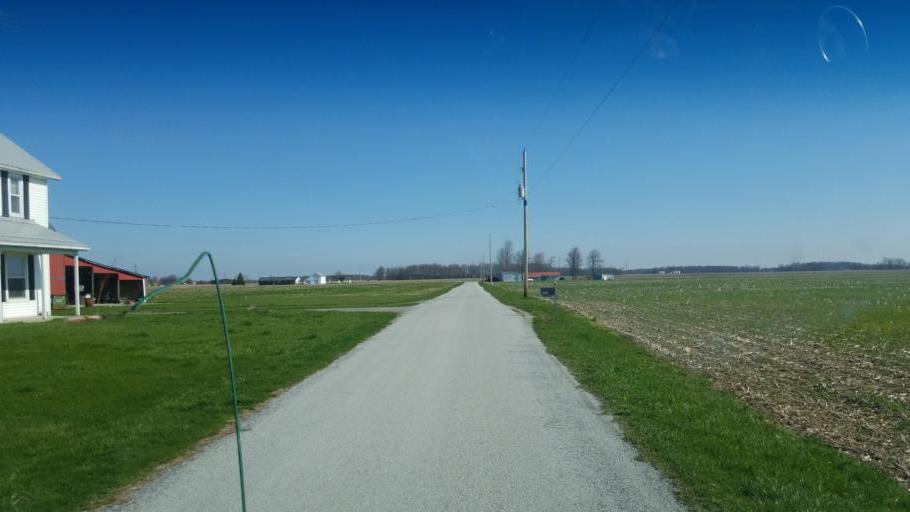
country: US
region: Ohio
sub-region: Hardin County
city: Kenton
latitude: 40.6989
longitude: -83.5602
